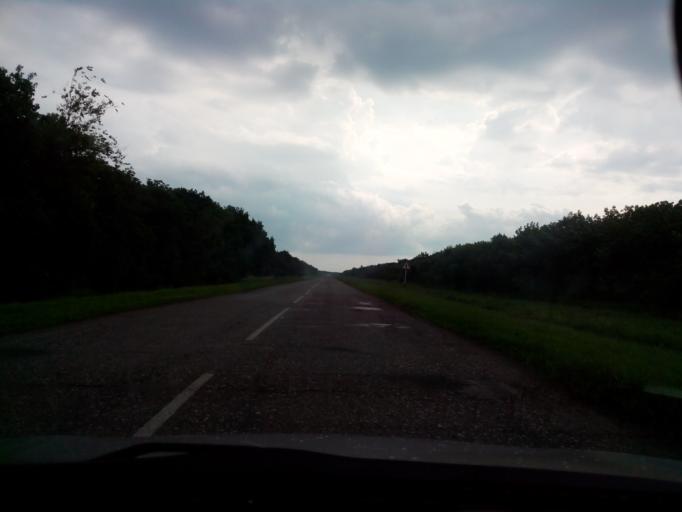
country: RU
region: Volgograd
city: Kumylzhenskaya
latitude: 49.9058
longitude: 42.8480
